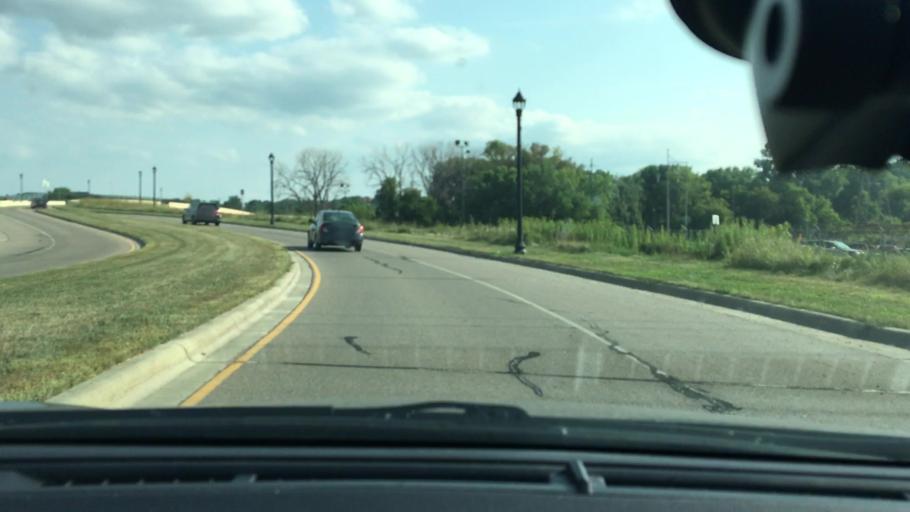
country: US
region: Minnesota
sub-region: Hennepin County
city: Minneapolis
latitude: 44.9771
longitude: -93.2961
